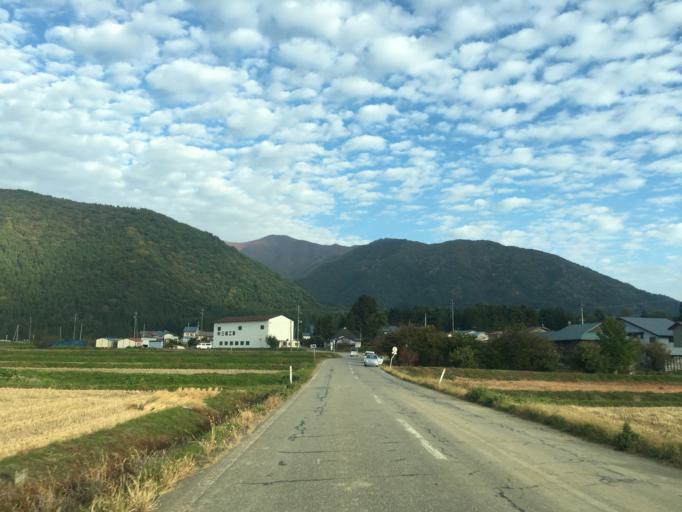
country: JP
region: Fukushima
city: Inawashiro
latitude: 37.5668
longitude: 140.1311
